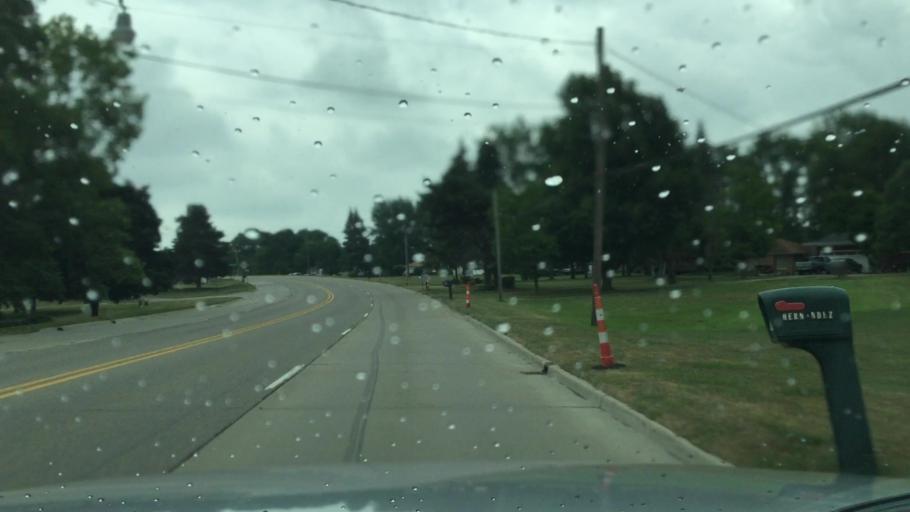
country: US
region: Michigan
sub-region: Genesee County
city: Flint
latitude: 43.0223
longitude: -83.7558
